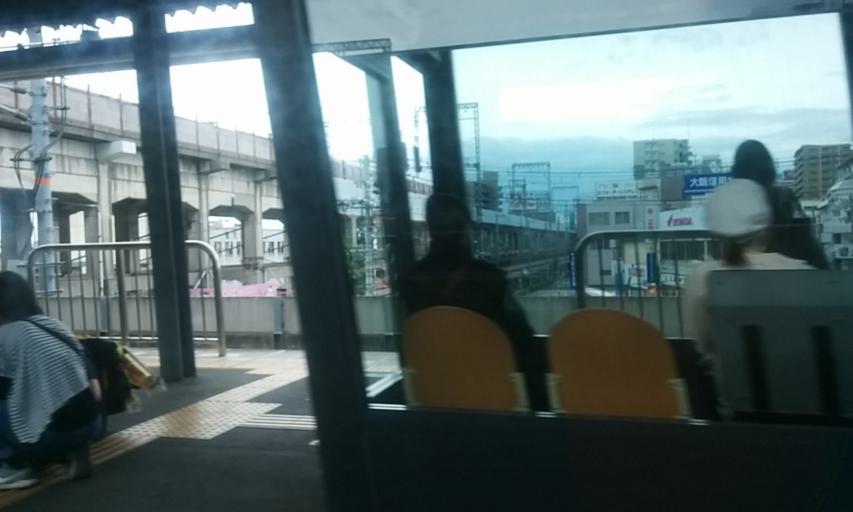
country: JP
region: Osaka
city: Yao
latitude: 34.6646
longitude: 135.5724
